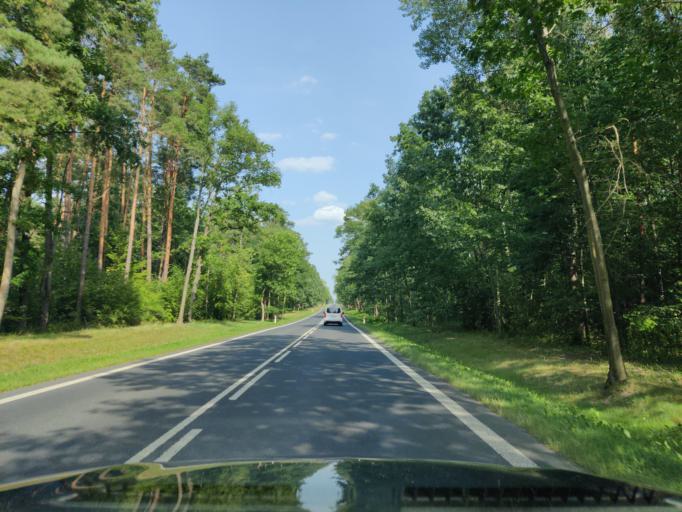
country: PL
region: Masovian Voivodeship
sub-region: Powiat makowski
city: Rzewnie
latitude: 52.8548
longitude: 21.2989
